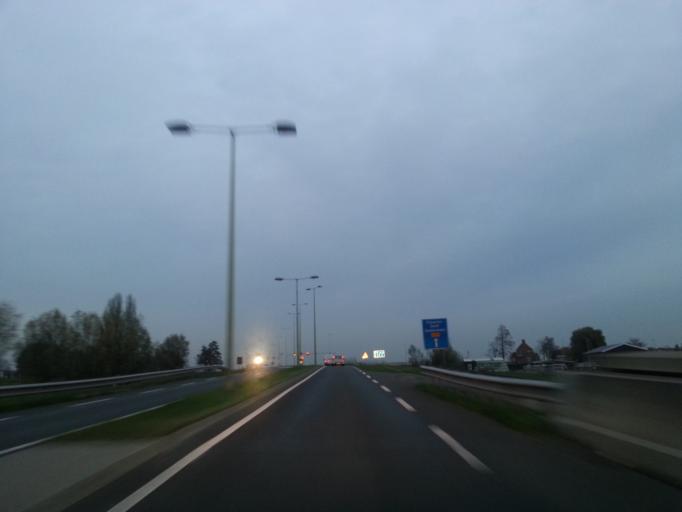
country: NL
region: South Holland
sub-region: Gemeente Lansingerland
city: Berkel en Rodenrijs
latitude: 51.9947
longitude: 4.4518
